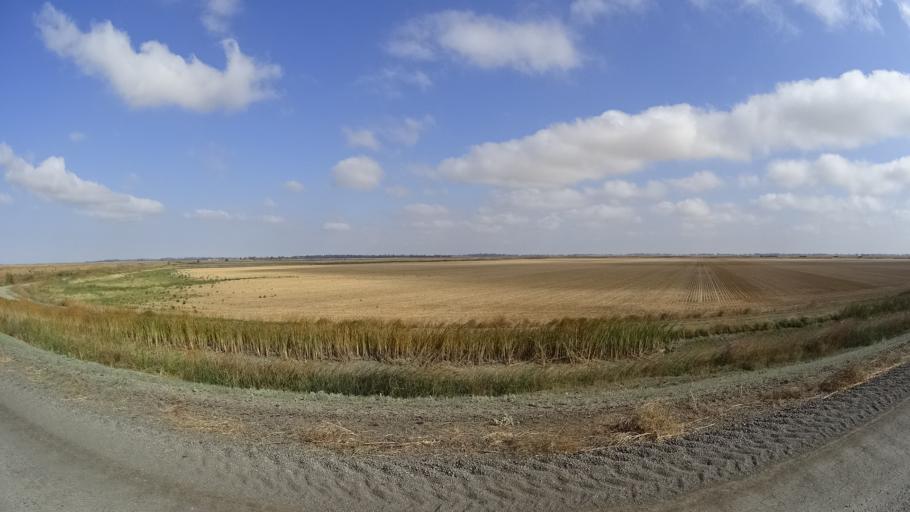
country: US
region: California
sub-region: Yolo County
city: Woodland
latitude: 38.8219
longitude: -121.7948
